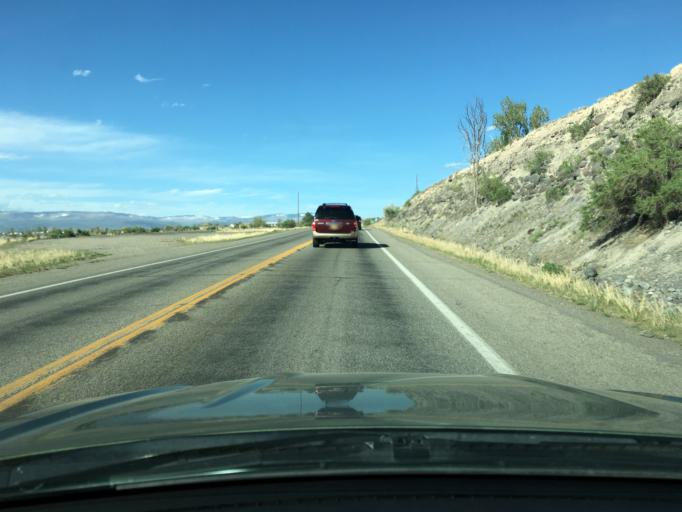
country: US
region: Colorado
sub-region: Delta County
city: Orchard City
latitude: 38.7837
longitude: -107.9961
